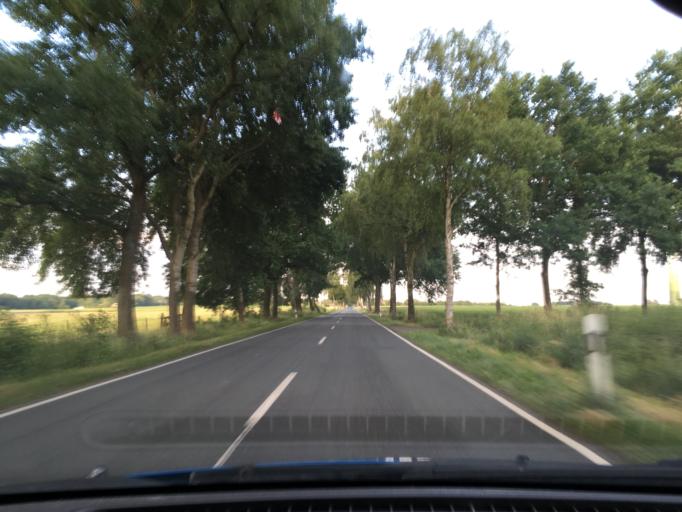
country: DE
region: Lower Saxony
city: Scharnhorst
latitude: 52.7221
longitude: 10.2983
